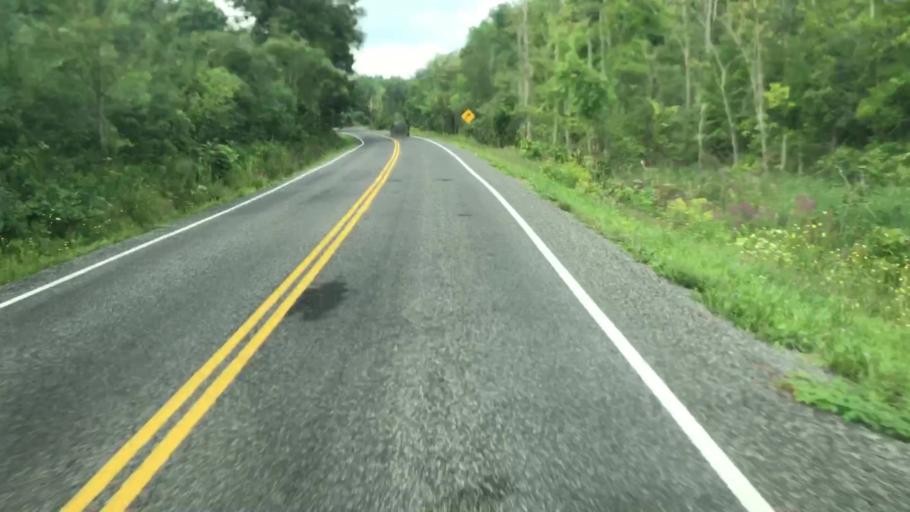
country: US
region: New York
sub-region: Onondaga County
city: Camillus
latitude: 43.0747
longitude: -76.3324
